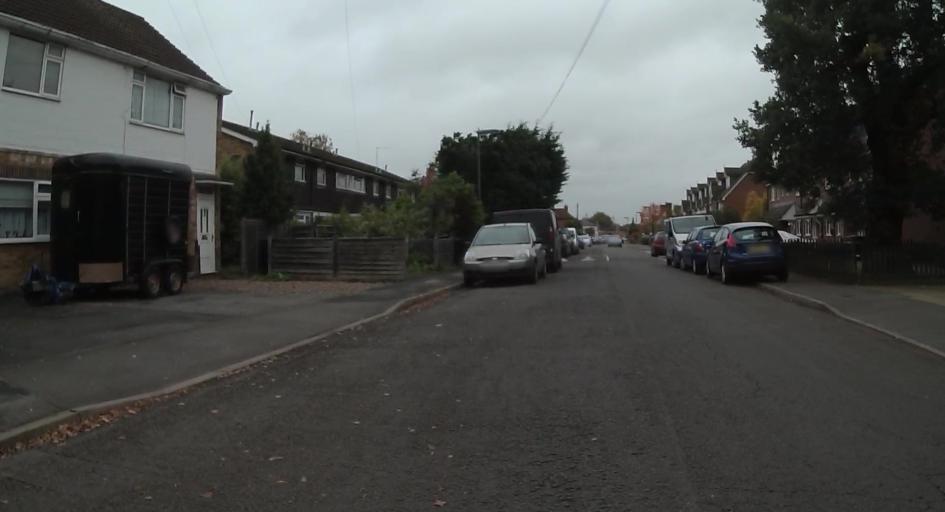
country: GB
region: England
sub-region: Surrey
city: Byfleet
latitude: 51.3420
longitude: -0.4805
